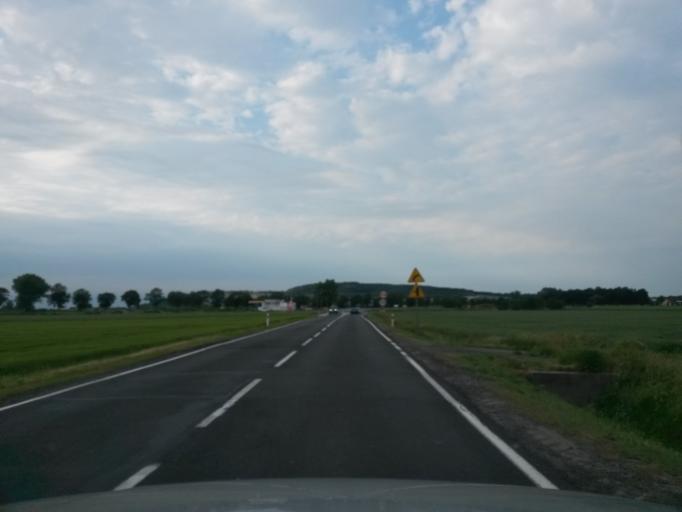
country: PL
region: Lower Silesian Voivodeship
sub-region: Powiat swidnicki
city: Strzegom
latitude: 50.9734
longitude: 16.3666
